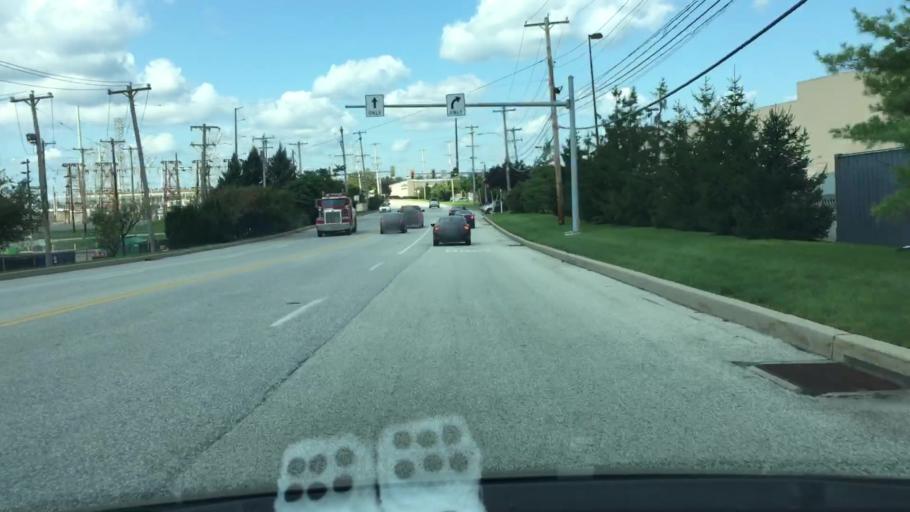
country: US
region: Pennsylvania
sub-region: Montgomery County
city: Plymouth Meeting
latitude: 40.1019
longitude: -75.2957
